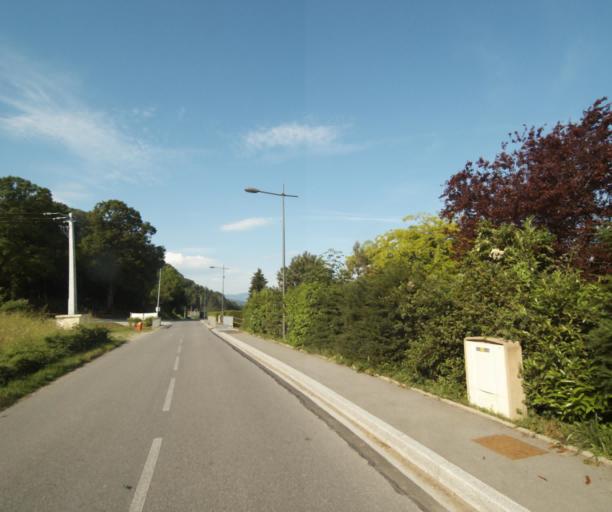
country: FR
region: Rhone-Alpes
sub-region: Departement de la Haute-Savoie
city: Lyaud
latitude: 46.3373
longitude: 6.5187
